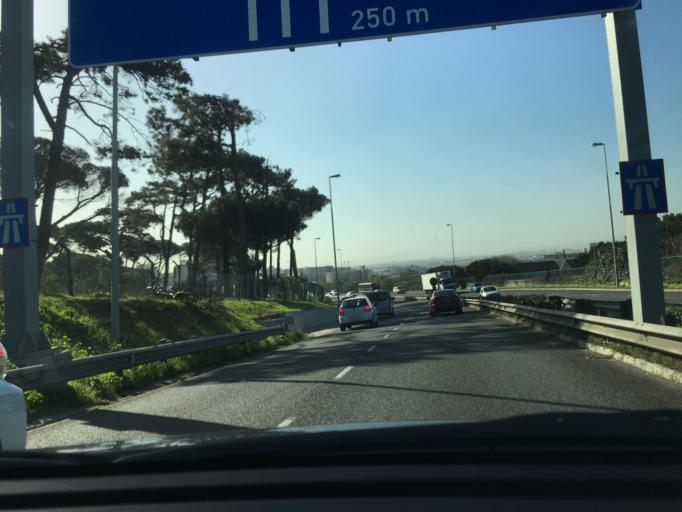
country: ZA
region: Western Cape
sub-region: City of Cape Town
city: Rosebank
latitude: -33.9506
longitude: 18.4666
